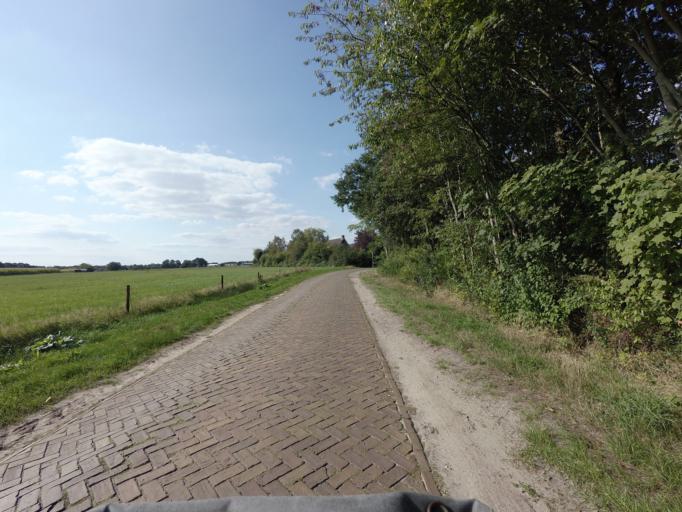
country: NL
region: Drenthe
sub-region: Gemeente Westerveld
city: Dwingeloo
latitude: 52.8342
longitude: 6.3923
